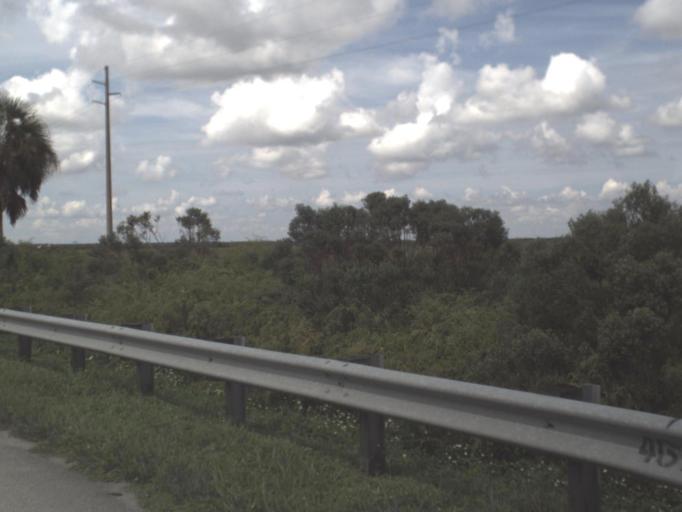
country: US
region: Florida
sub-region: Highlands County
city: Lake Placid
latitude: 27.2090
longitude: -81.2174
